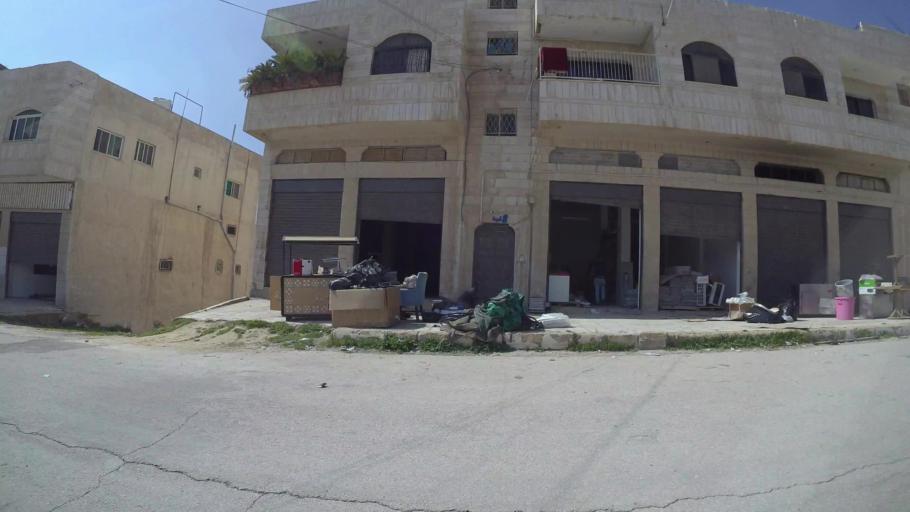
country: JO
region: Amman
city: Al Bunayyat ash Shamaliyah
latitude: 31.9023
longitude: 35.9021
